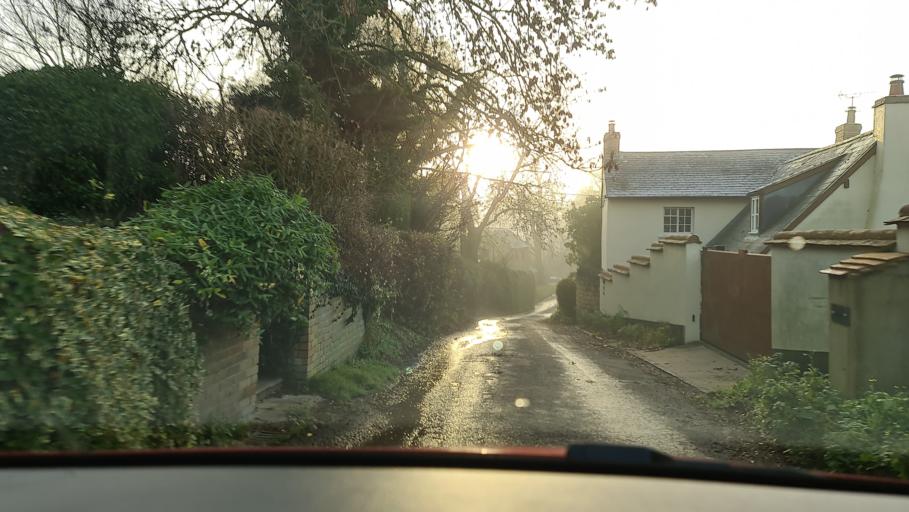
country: GB
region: England
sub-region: Buckinghamshire
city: Haddenham
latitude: 51.8054
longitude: -0.9395
